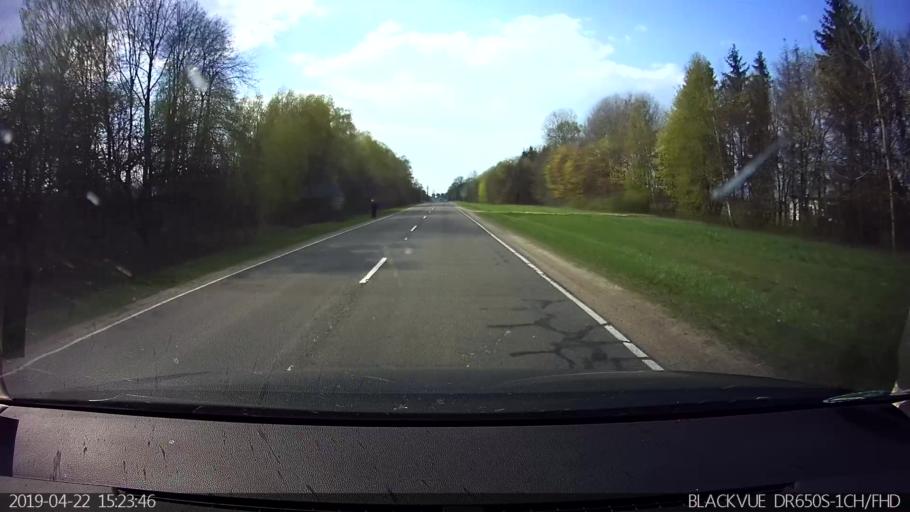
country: BY
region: Brest
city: Vysokaye
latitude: 52.3572
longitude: 23.4199
